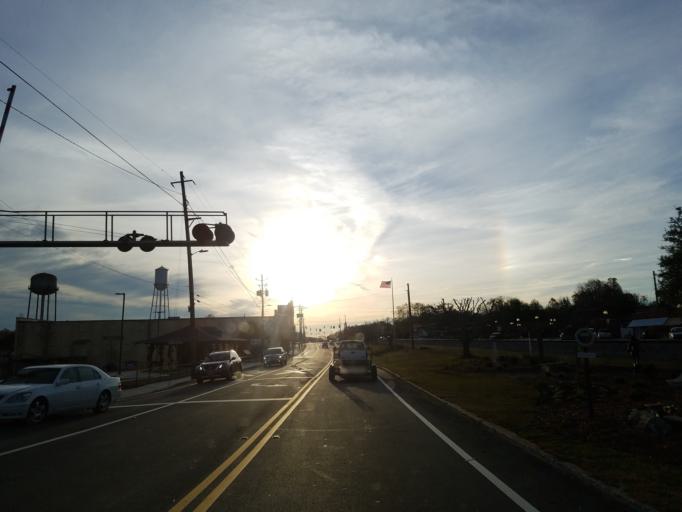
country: US
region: Georgia
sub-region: Haralson County
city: Bremen
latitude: 33.7206
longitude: -85.1462
